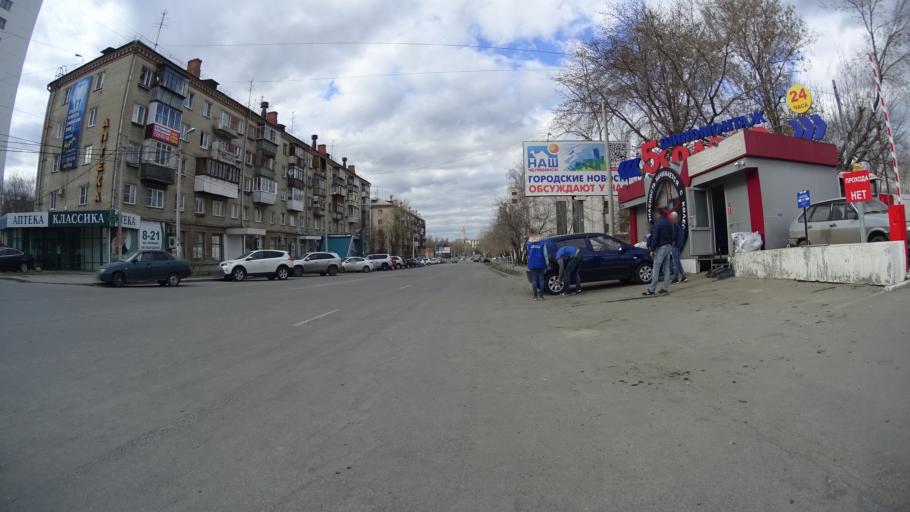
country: RU
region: Chelyabinsk
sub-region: Gorod Chelyabinsk
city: Chelyabinsk
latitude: 55.1607
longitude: 61.3864
